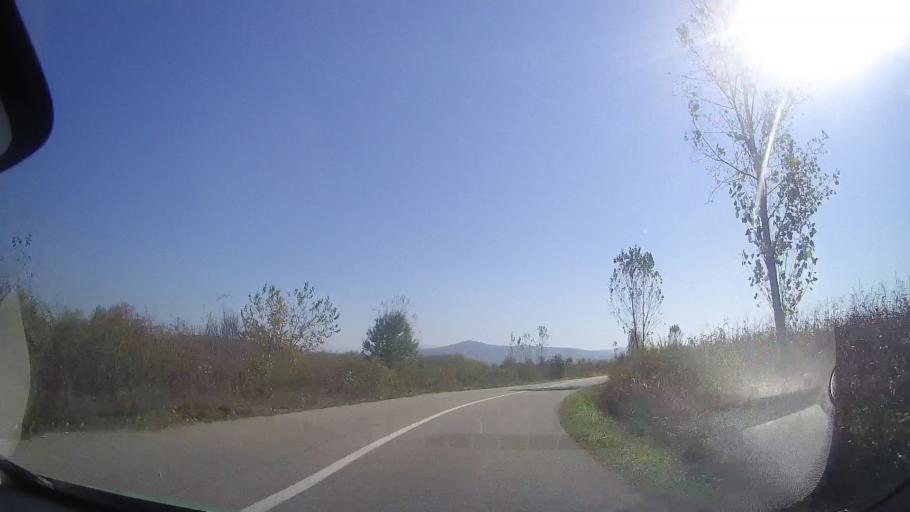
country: RO
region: Timis
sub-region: Comuna Traian Vuia
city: Traian Vuia
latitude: 45.7819
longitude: 22.0494
